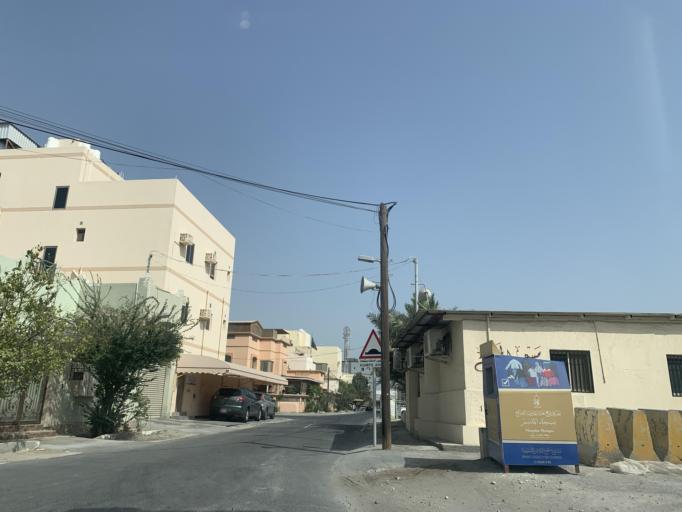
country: BH
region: Northern
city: Madinat `Isa
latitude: 26.1891
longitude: 50.5476
